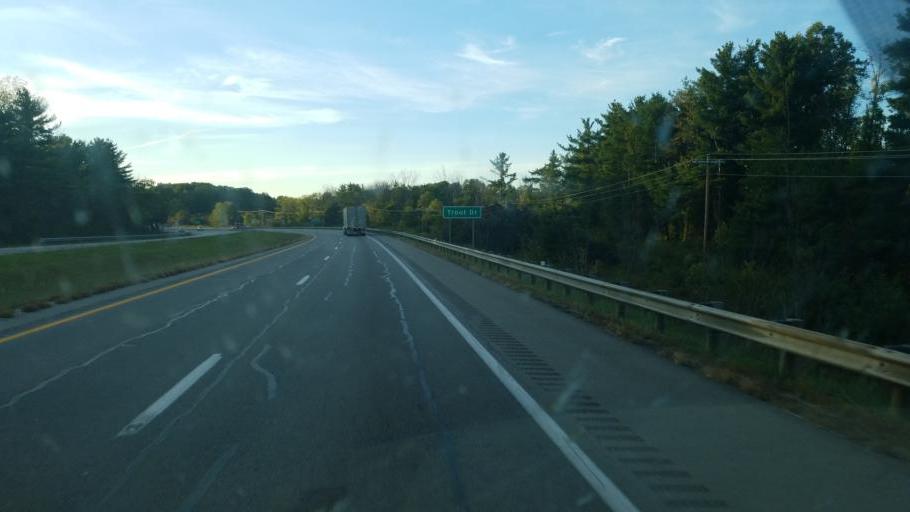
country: US
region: Ohio
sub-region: Richland County
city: Lincoln Heights
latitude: 40.7855
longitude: -82.3891
